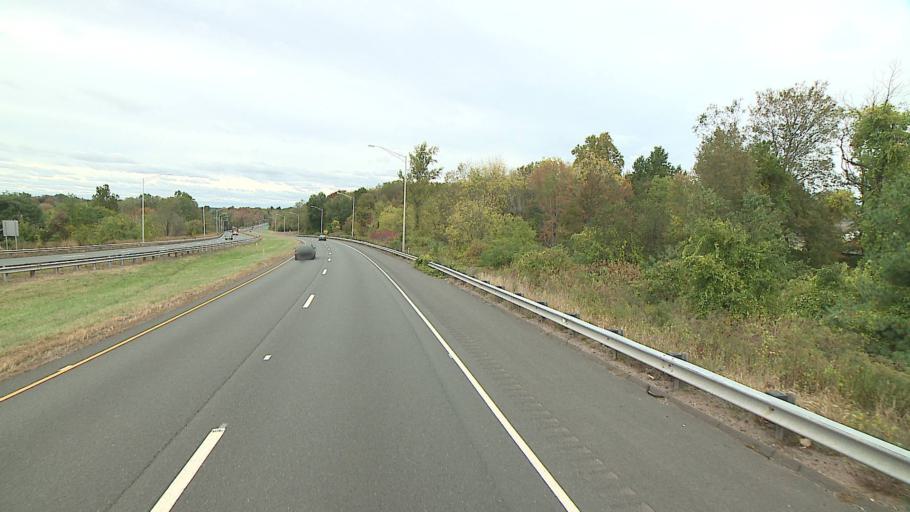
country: US
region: Connecticut
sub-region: Middlesex County
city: Middletown
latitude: 41.5355
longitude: -72.6191
